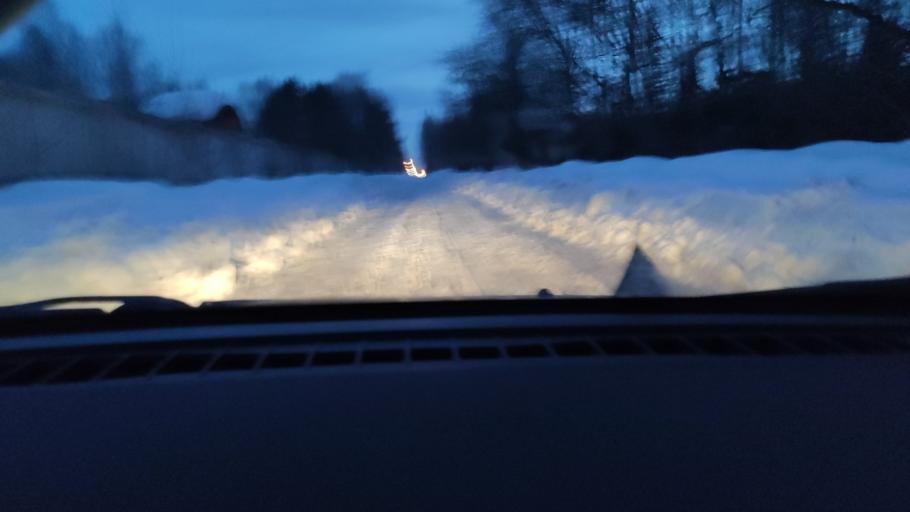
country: RU
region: Perm
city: Kondratovo
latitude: 58.0672
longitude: 56.1266
